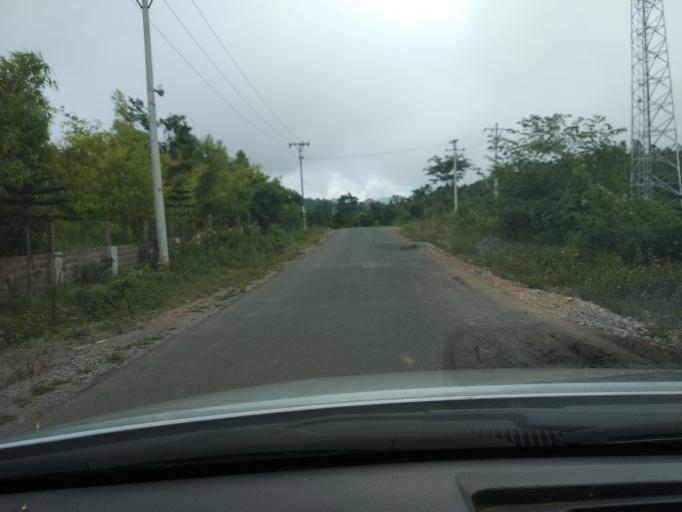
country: MM
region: Mandalay
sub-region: Pyin Oo Lwin District
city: Pyin Oo Lwin
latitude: 21.9213
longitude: 96.3779
